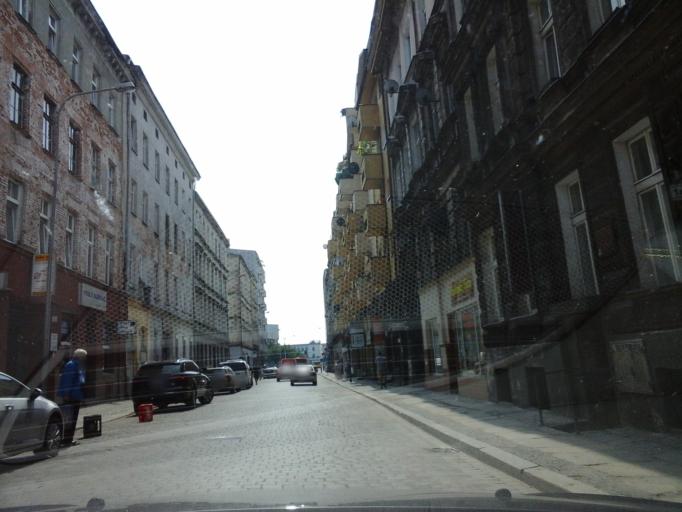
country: PL
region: Lower Silesian Voivodeship
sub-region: Powiat wroclawski
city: Wroclaw
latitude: 51.1030
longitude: 17.0402
